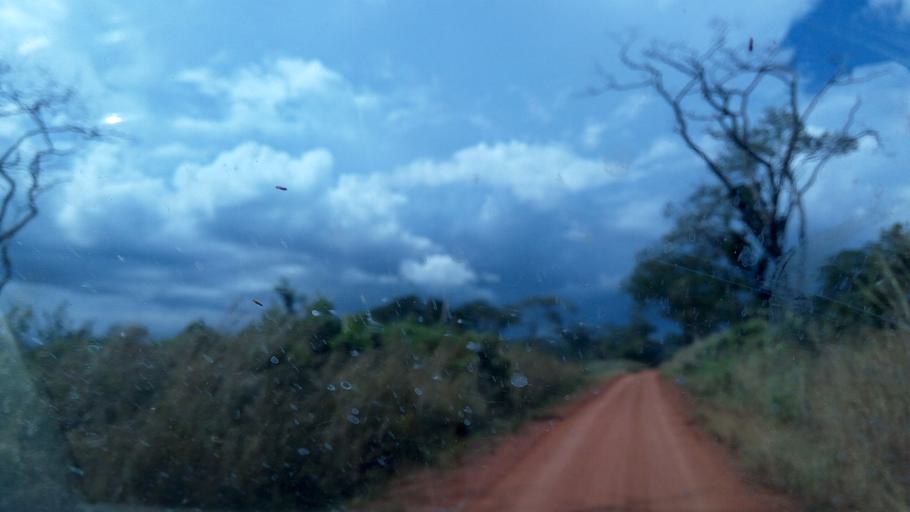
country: ZM
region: Northern
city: Kaputa
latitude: -8.1460
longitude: 29.1080
